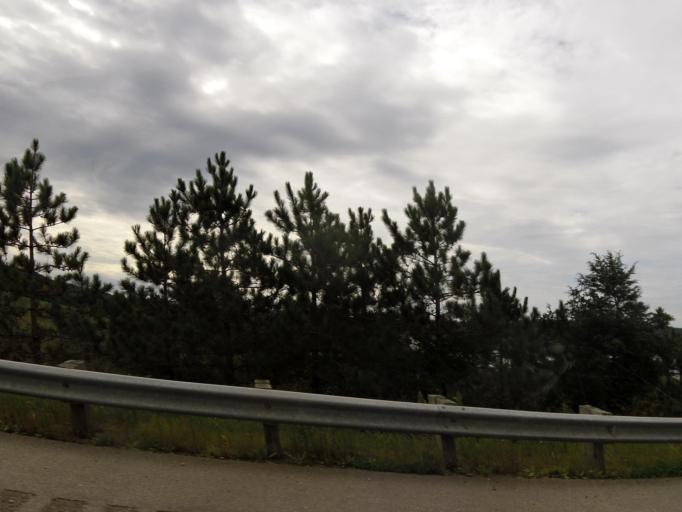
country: US
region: Wisconsin
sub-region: La Crosse County
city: Bangor
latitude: 43.8859
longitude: -90.9986
